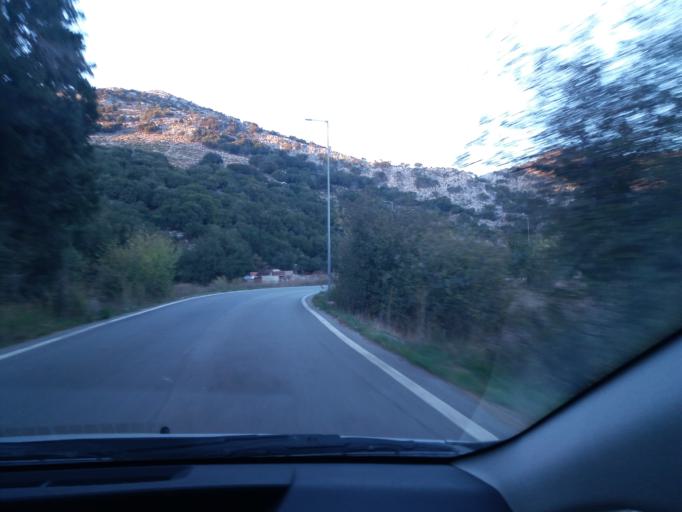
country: GR
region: Crete
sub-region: Nomos Irakleiou
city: Mokhos
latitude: 35.2030
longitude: 25.4745
